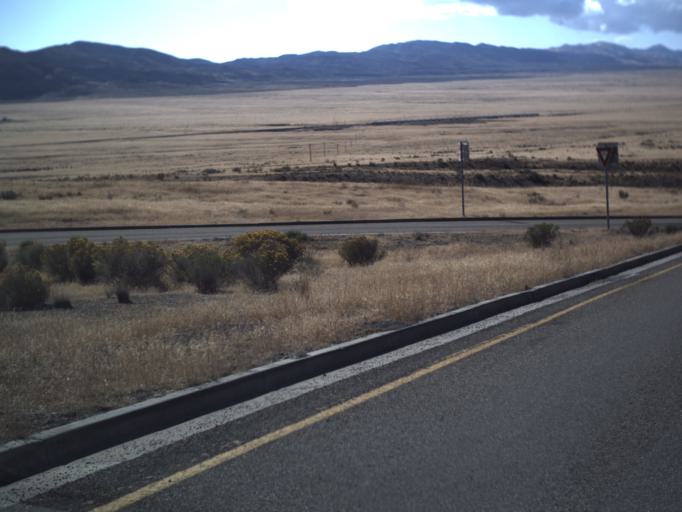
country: US
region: Utah
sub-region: Tooele County
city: Grantsville
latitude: 40.7618
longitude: -113.0113
